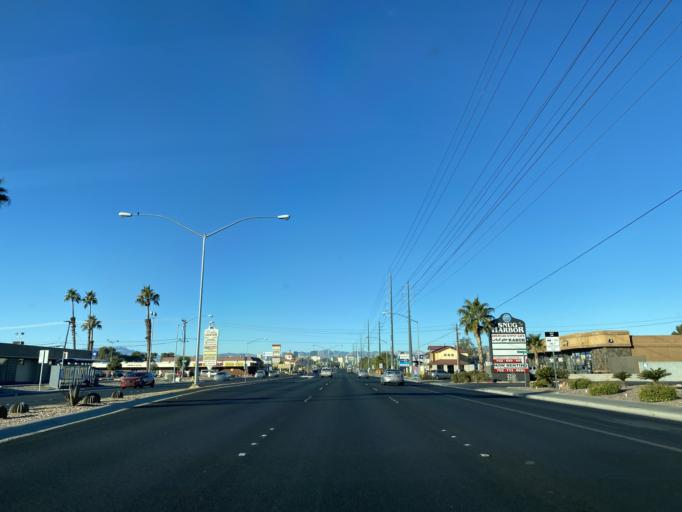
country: US
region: Nevada
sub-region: Clark County
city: Winchester
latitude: 36.1150
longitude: -115.1120
